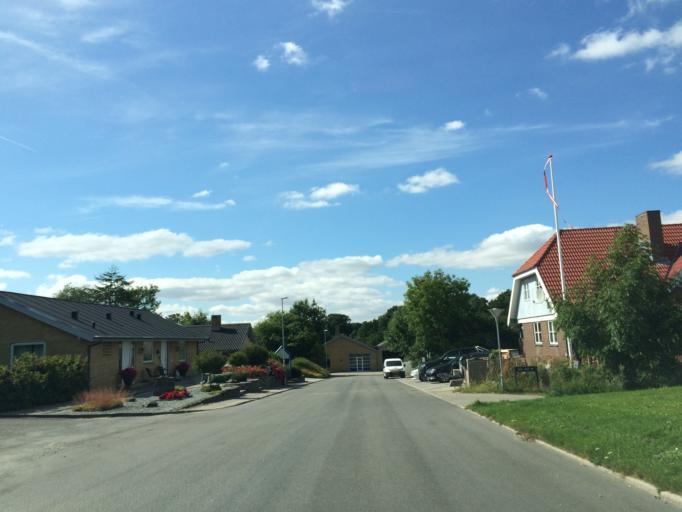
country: DK
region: Central Jutland
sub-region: Syddjurs Kommune
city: Ronde
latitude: 56.3020
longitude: 10.4624
